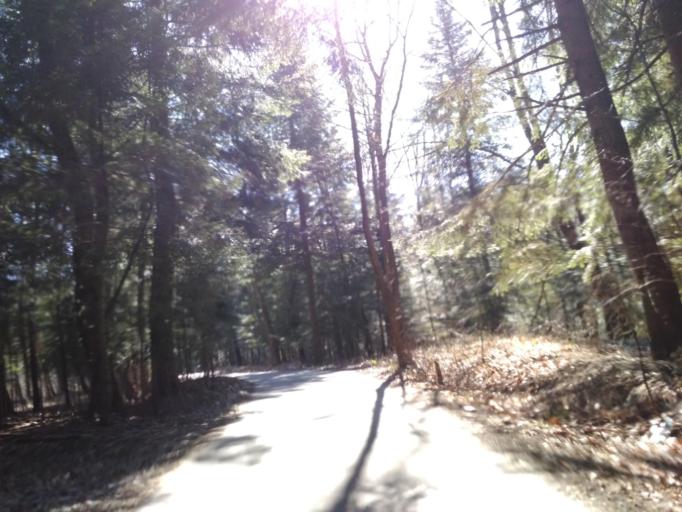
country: PL
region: Subcarpathian Voivodeship
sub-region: Powiat brzozowski
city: Zmiennica
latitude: 49.7076
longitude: 21.9666
